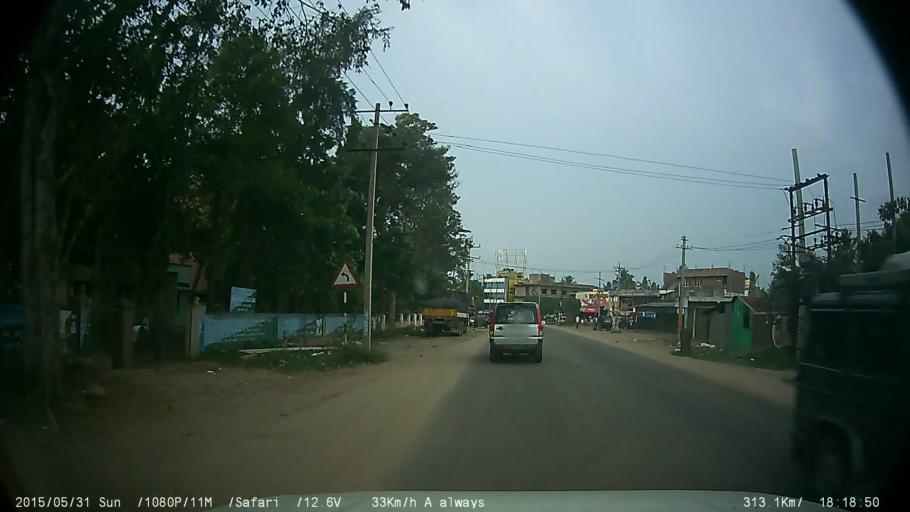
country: IN
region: Karnataka
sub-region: Mysore
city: Nanjangud
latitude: 12.1215
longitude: 76.6766
